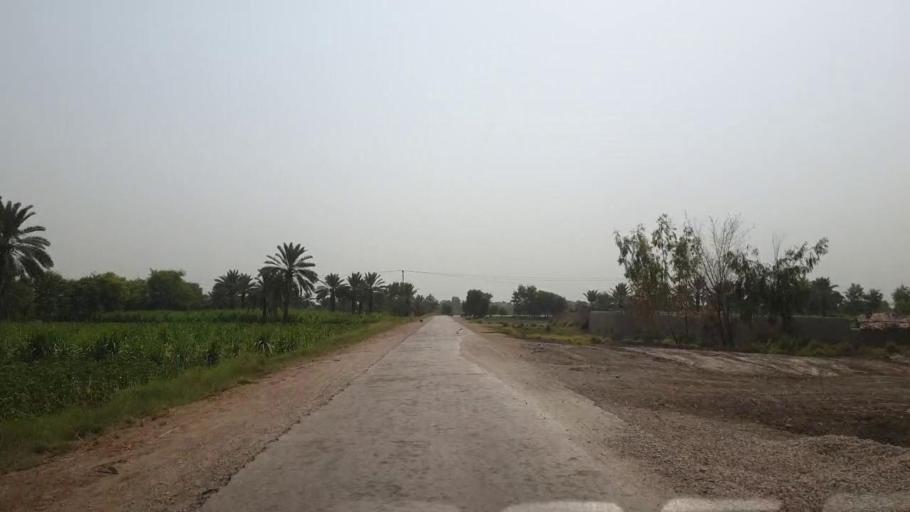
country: PK
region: Sindh
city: Gambat
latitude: 27.4320
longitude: 68.5308
